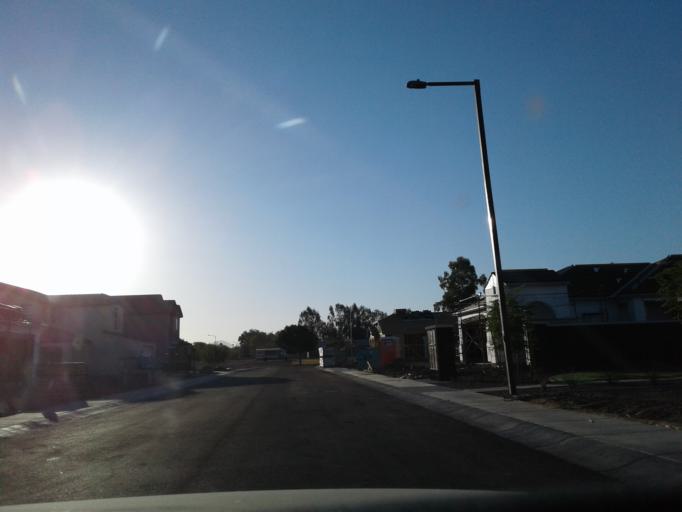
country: US
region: Arizona
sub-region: Maricopa County
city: Glendale
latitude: 33.6270
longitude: -112.1069
